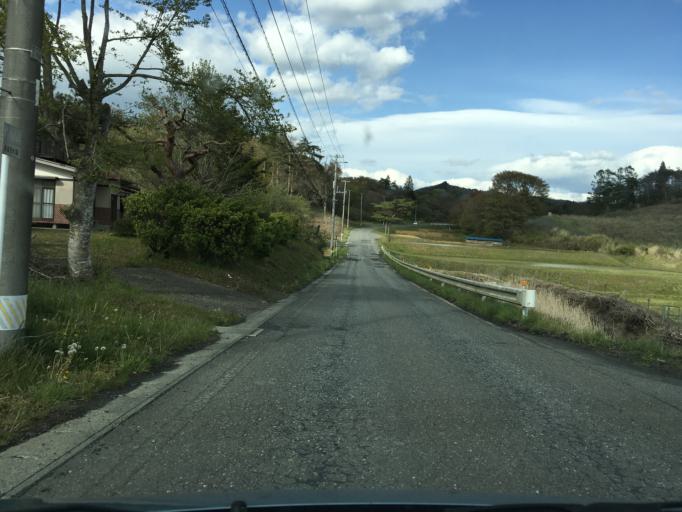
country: JP
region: Iwate
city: Ichinoseki
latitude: 38.7922
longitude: 141.4129
